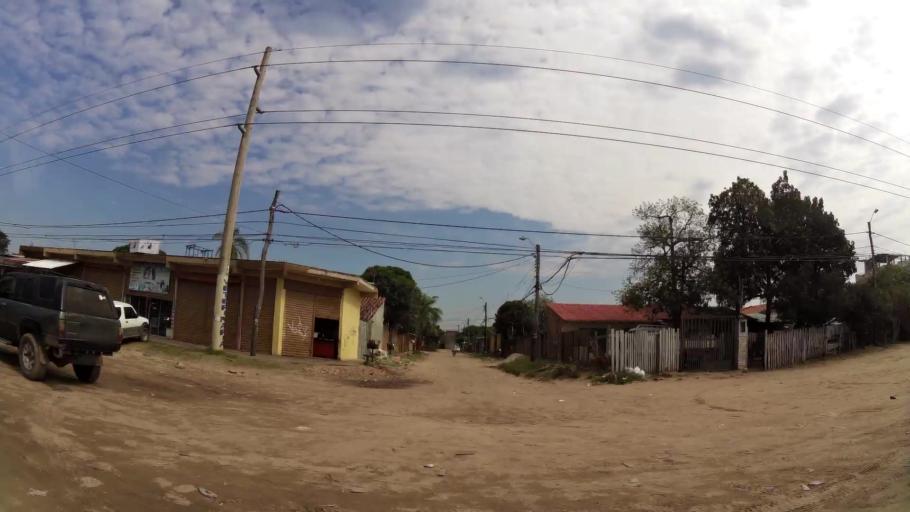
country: BO
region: Santa Cruz
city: Santa Cruz de la Sierra
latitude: -17.7358
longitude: -63.1789
